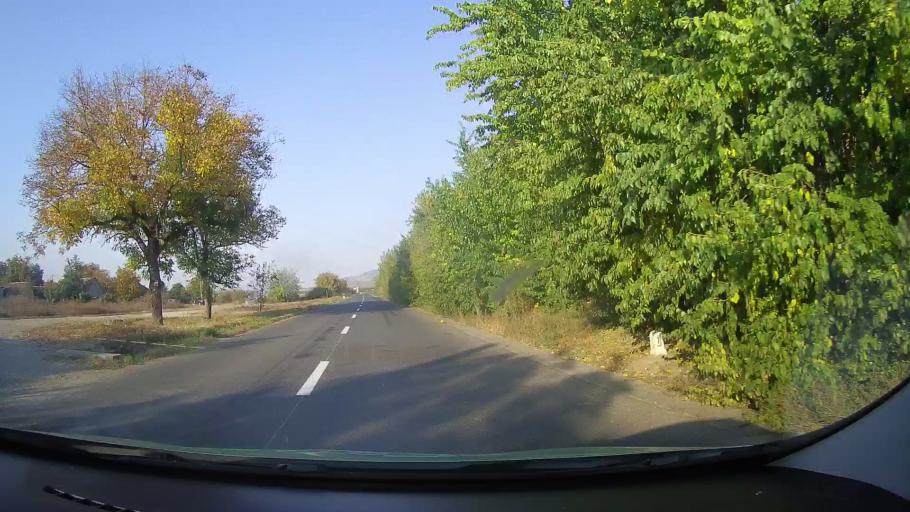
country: RO
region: Arad
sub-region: Comuna Covasint
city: Covasint
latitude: 46.2097
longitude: 21.6109
